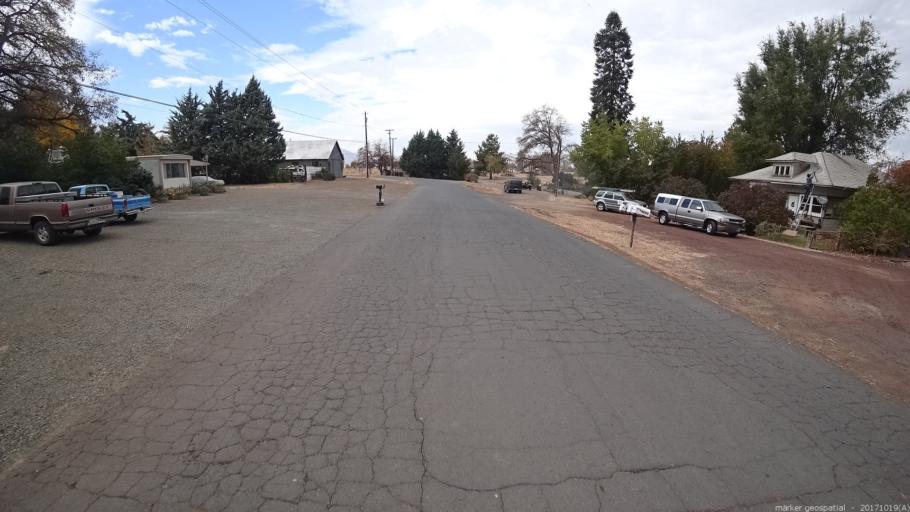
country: US
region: California
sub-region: Shasta County
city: Burney
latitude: 41.0482
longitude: -121.4020
